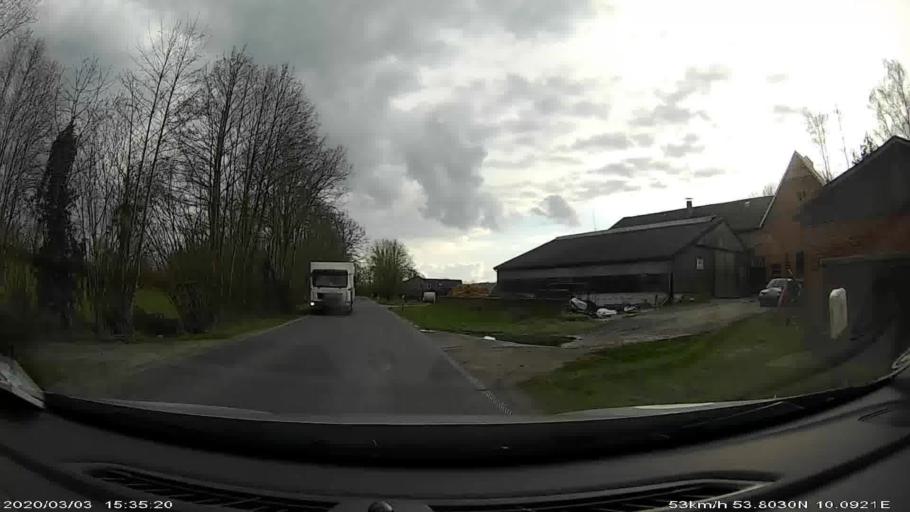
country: DE
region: Schleswig-Holstein
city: Huttblek
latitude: 53.8036
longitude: 10.0924
